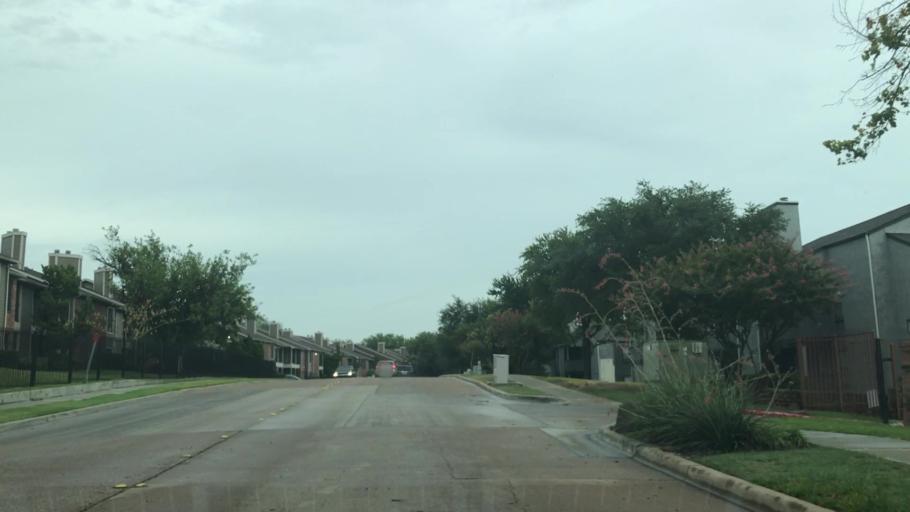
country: US
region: Texas
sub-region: Denton County
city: Lewisville
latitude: 33.0191
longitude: -96.9897
